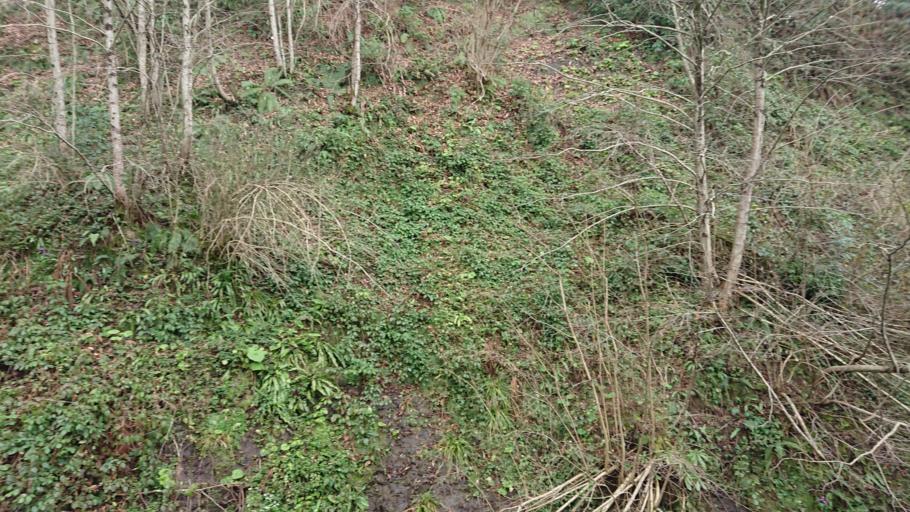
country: TR
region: Rize
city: Rize
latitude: 40.9803
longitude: 40.4945
